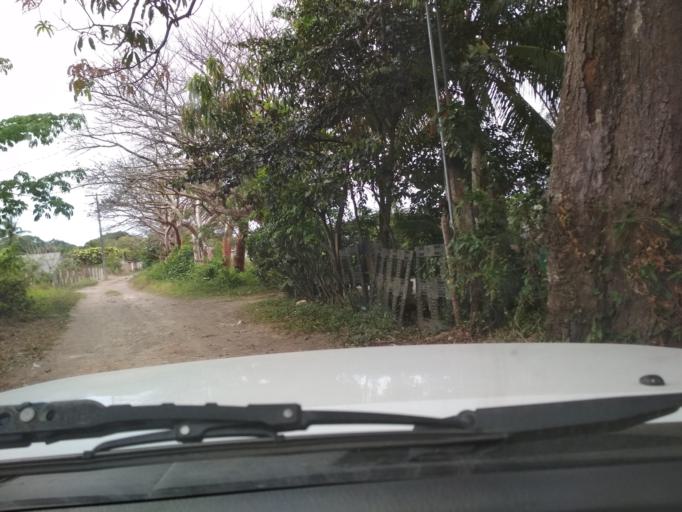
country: MX
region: Veracruz
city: El Tejar
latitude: 19.0718
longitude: -96.1509
